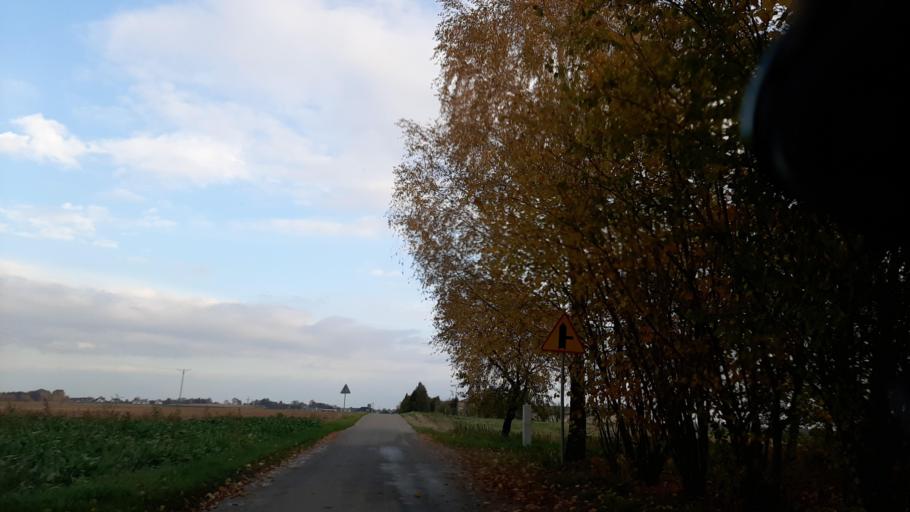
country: PL
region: Lublin Voivodeship
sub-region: Powiat lubelski
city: Garbow
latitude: 51.3428
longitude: 22.3192
